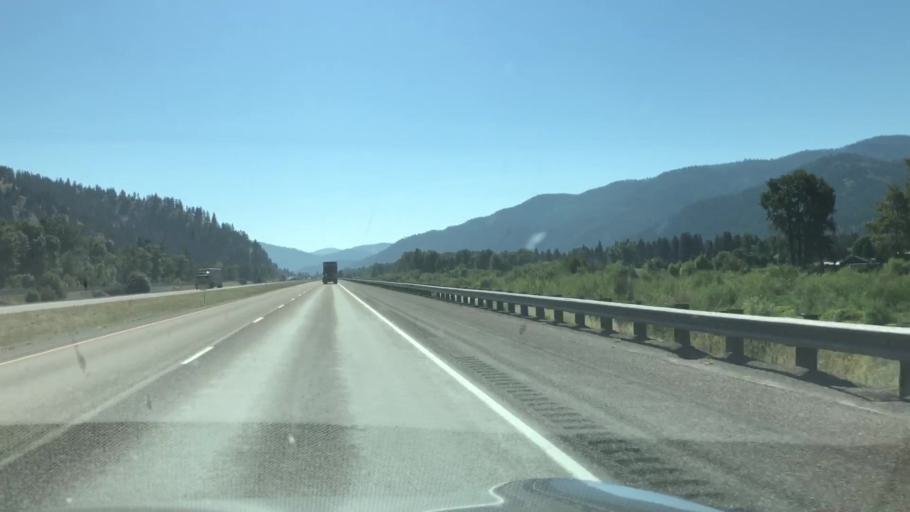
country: US
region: Montana
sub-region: Missoula County
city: Bonner-West Riverside
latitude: 46.8225
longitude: -113.8057
